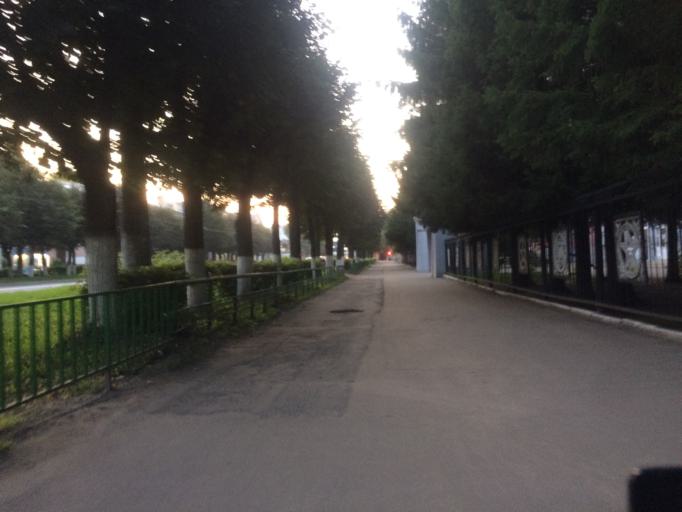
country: RU
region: Mariy-El
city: Yoshkar-Ola
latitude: 56.6356
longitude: 47.8758
